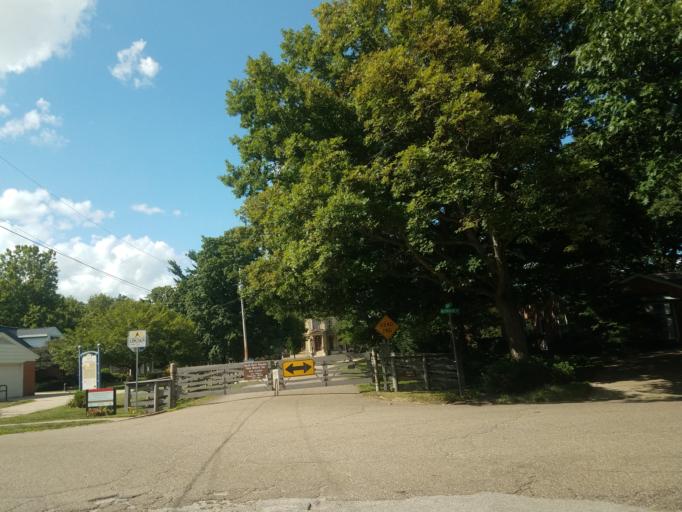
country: US
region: Illinois
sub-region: McLean County
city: Bloomington
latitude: 40.4815
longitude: -88.9806
